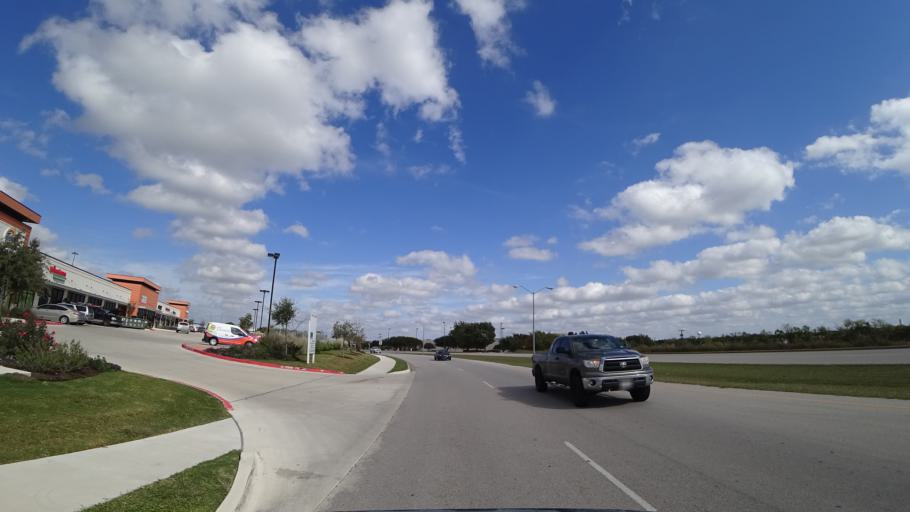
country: US
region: Texas
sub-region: Travis County
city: Windemere
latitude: 30.4800
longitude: -97.6614
